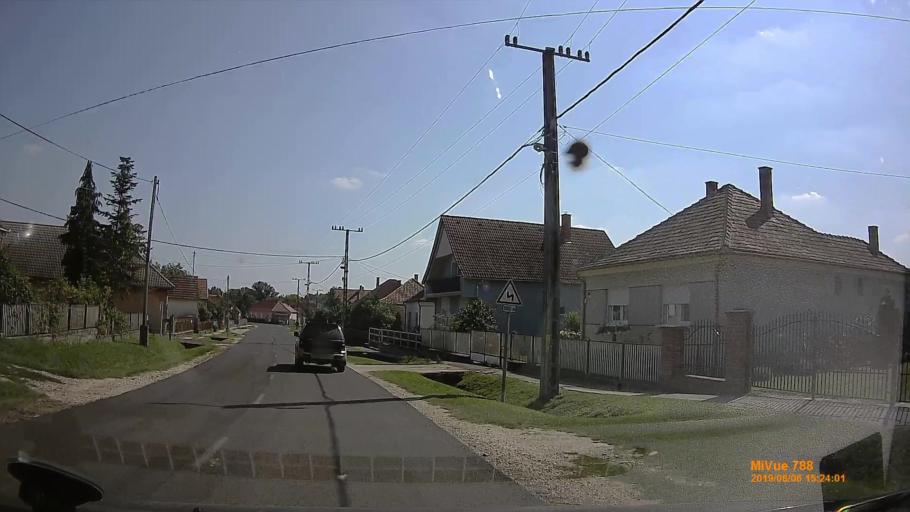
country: HR
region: Koprivnicko-Krizevacka
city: Drnje
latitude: 46.2576
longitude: 16.9408
